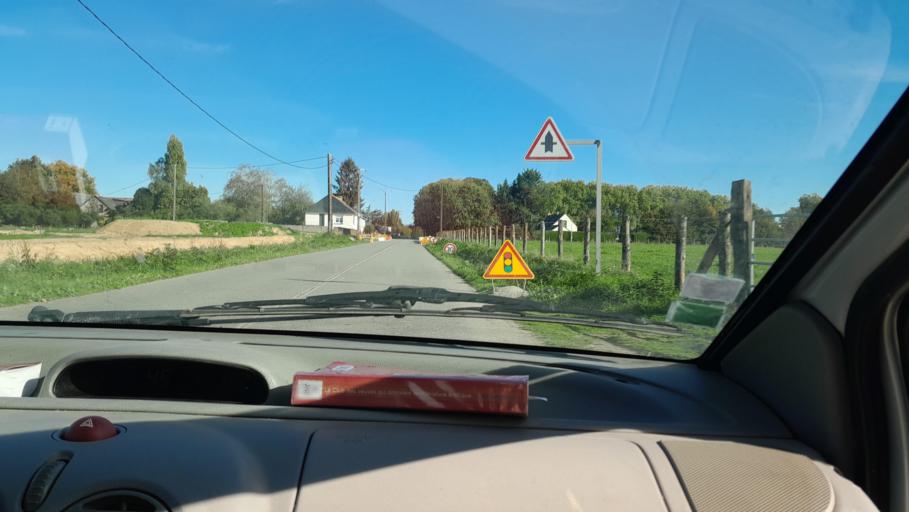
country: FR
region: Brittany
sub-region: Departement d'Ille-et-Vilaine
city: Etrelles
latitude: 48.0570
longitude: -1.1827
